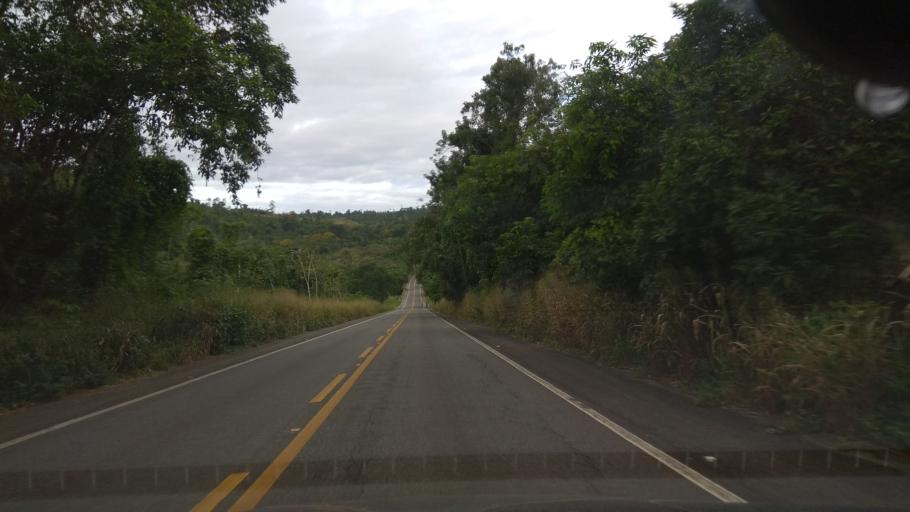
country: BR
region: Bahia
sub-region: Ibirapitanga
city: Ibirapitanga
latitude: -14.2457
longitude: -39.3794
